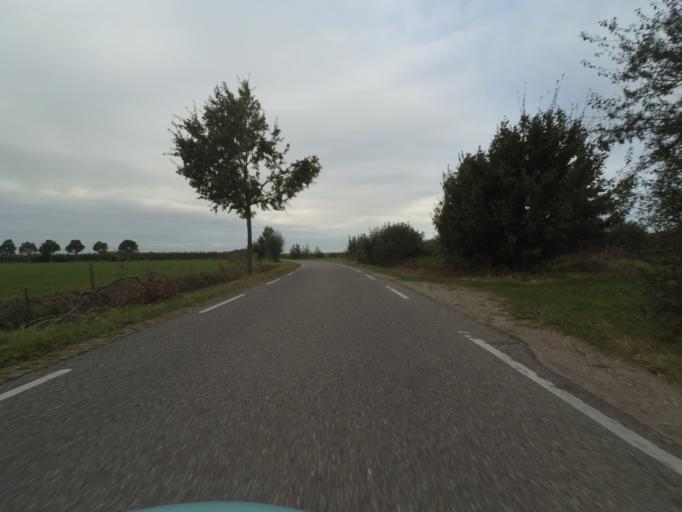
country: NL
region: Utrecht
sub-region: Gemeente Wijk bij Duurstede
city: Wijk bij Duurstede
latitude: 51.9931
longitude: 5.3366
